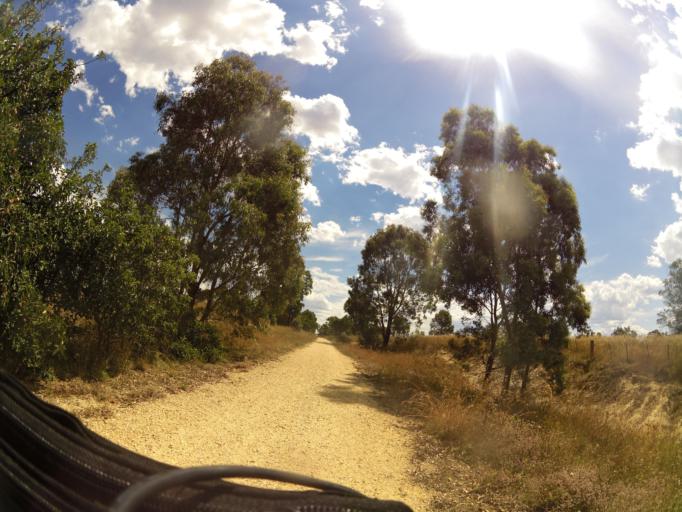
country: AU
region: Victoria
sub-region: Wellington
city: Heyfield
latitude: -37.9763
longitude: 146.7604
